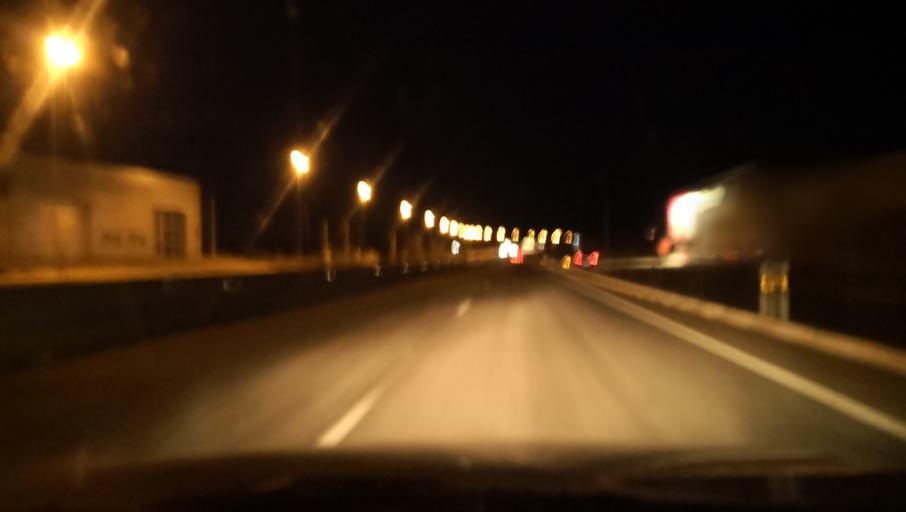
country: ES
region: Castille and Leon
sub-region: Provincia de Zamora
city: Valcabado
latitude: 41.5338
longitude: -5.7610
